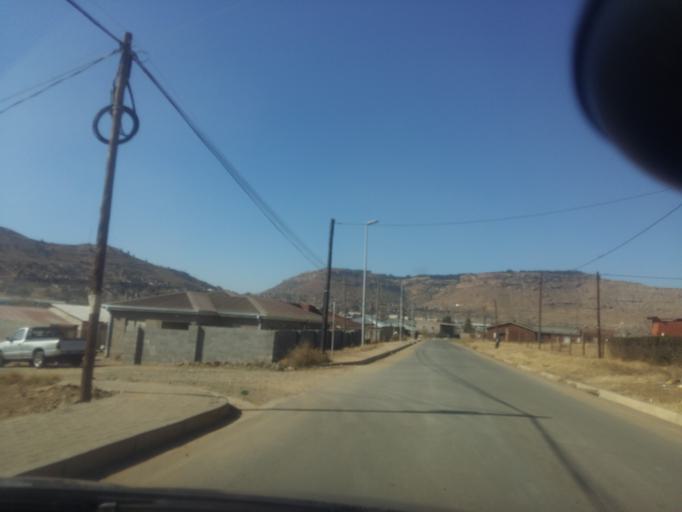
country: LS
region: Maseru
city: Maseru
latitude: -29.3374
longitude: 27.4508
